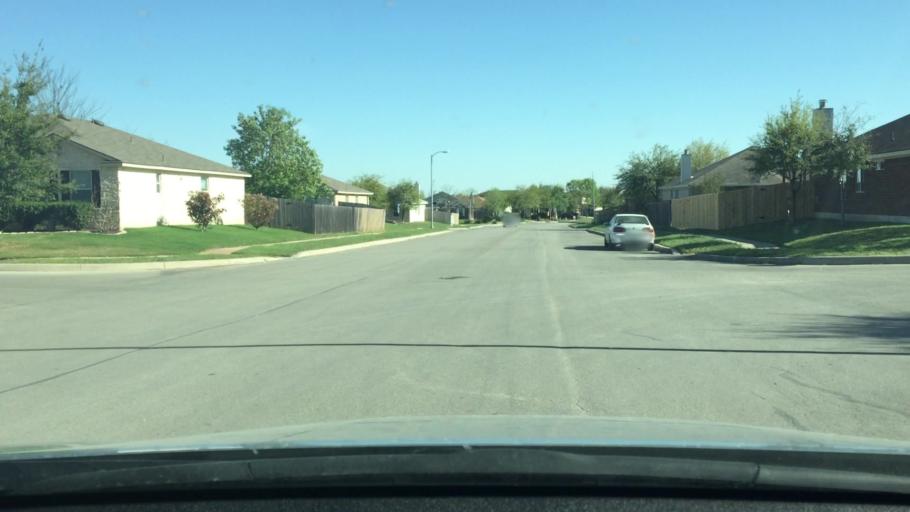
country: US
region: Texas
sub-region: Bexar County
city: Converse
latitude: 29.4696
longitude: -98.3221
